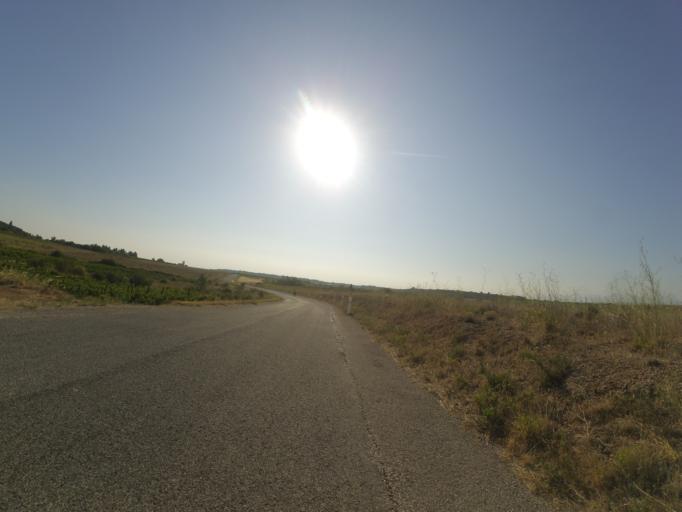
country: FR
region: Languedoc-Roussillon
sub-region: Departement des Pyrenees-Orientales
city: Baixas
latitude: 42.7483
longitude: 2.7955
